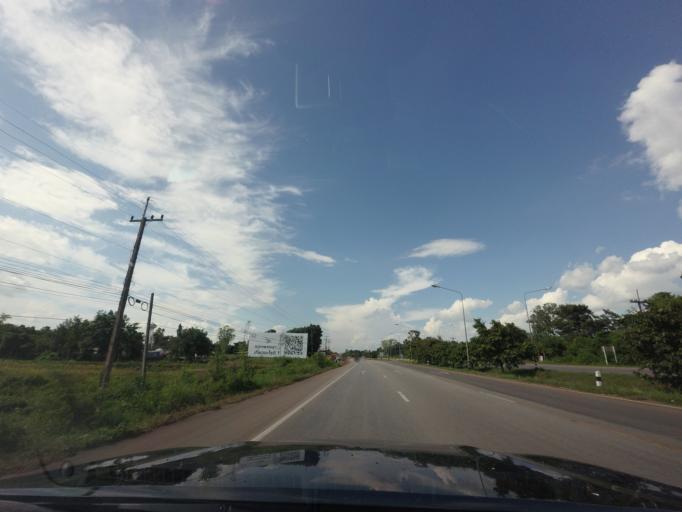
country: TH
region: Nong Khai
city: Sa Khrai
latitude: 17.6695
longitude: 102.7907
